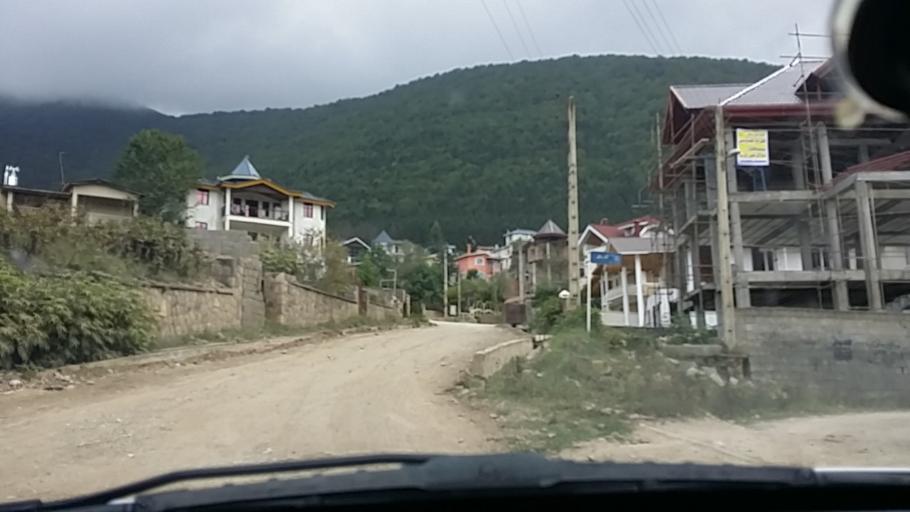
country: IR
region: Mazandaran
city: `Abbasabad
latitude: 36.4936
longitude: 51.1653
